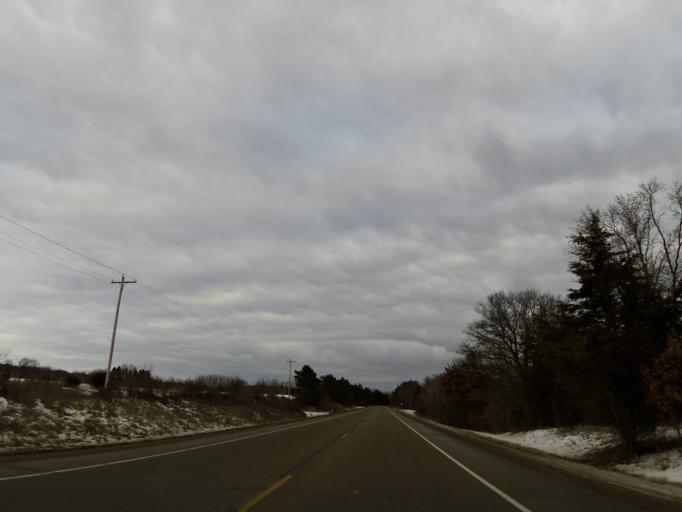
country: US
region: Wisconsin
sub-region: Saint Croix County
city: North Hudson
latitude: 45.0236
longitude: -92.7461
